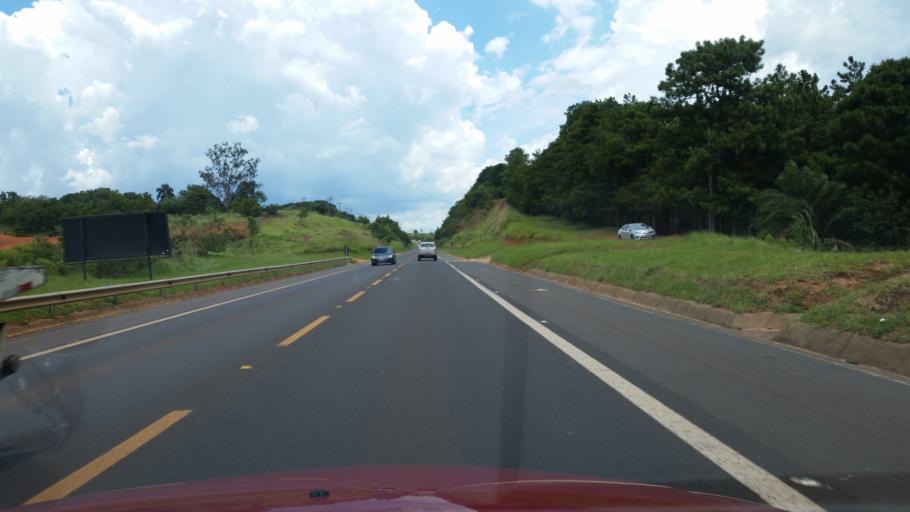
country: BR
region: Sao Paulo
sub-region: Itai
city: Itai
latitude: -23.2735
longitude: -49.0170
